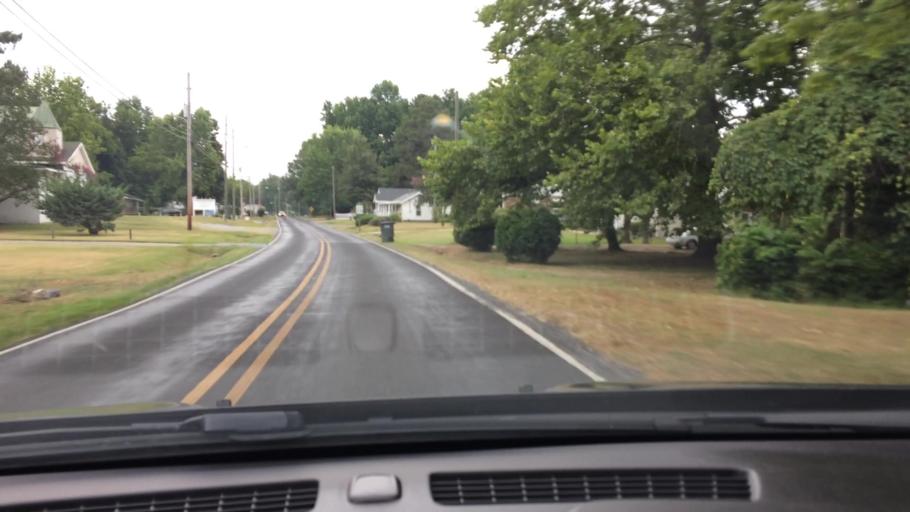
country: US
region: North Carolina
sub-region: Pitt County
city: Ayden
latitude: 35.4633
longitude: -77.4154
